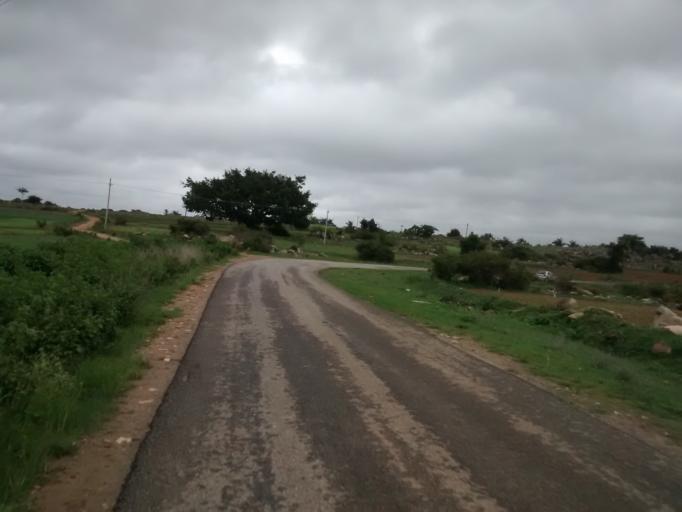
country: IN
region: Karnataka
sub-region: Hassan
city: Hassan
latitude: 12.9383
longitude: 76.1740
